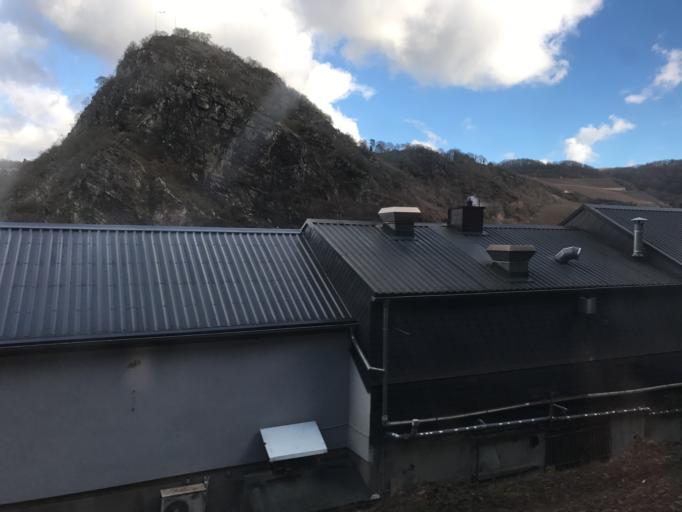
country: DE
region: Rheinland-Pfalz
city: Urbar
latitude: 50.1370
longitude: 7.7260
